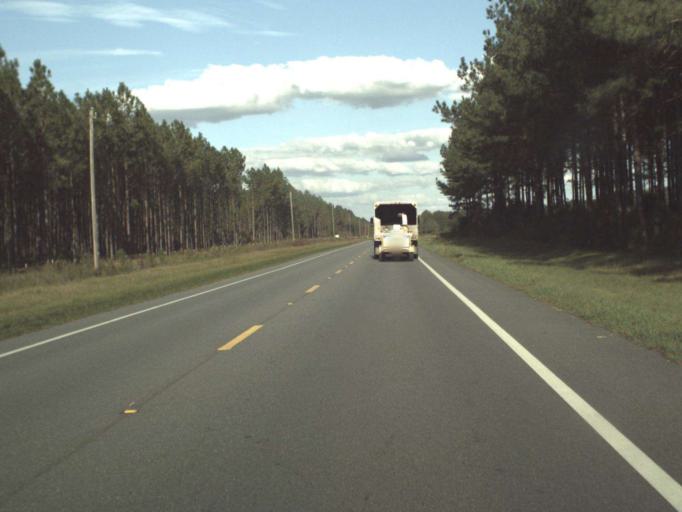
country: US
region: Florida
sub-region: Holmes County
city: Bonifay
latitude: 30.6523
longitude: -85.6714
